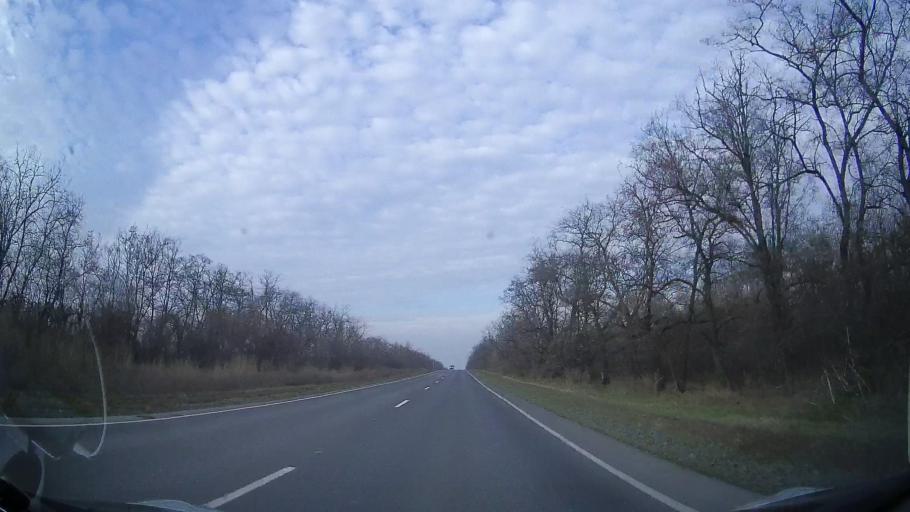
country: RU
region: Rostov
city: Bagayevskaya
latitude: 47.1211
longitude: 40.2767
